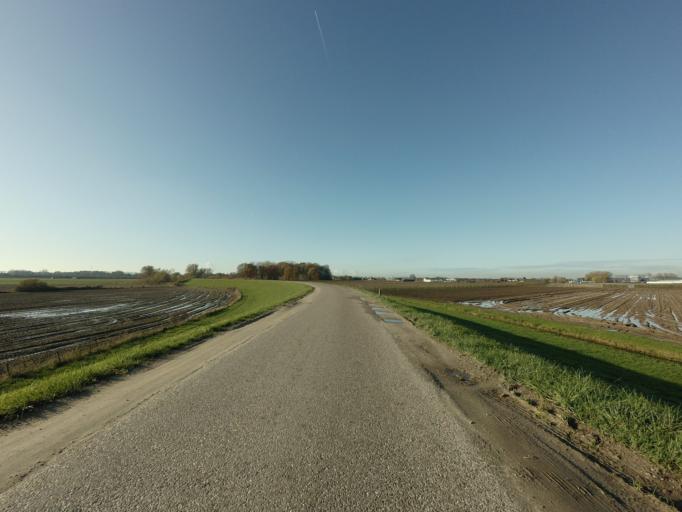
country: NL
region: Gelderland
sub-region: Gemeente Maasdriel
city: Hedel
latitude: 51.7495
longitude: 5.2859
